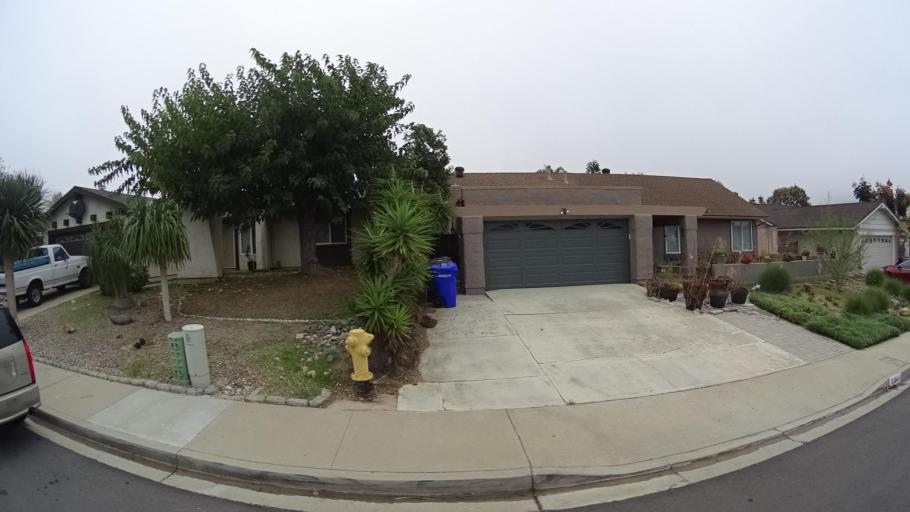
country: US
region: California
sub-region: San Diego County
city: Rancho San Diego
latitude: 32.7309
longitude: -116.9584
